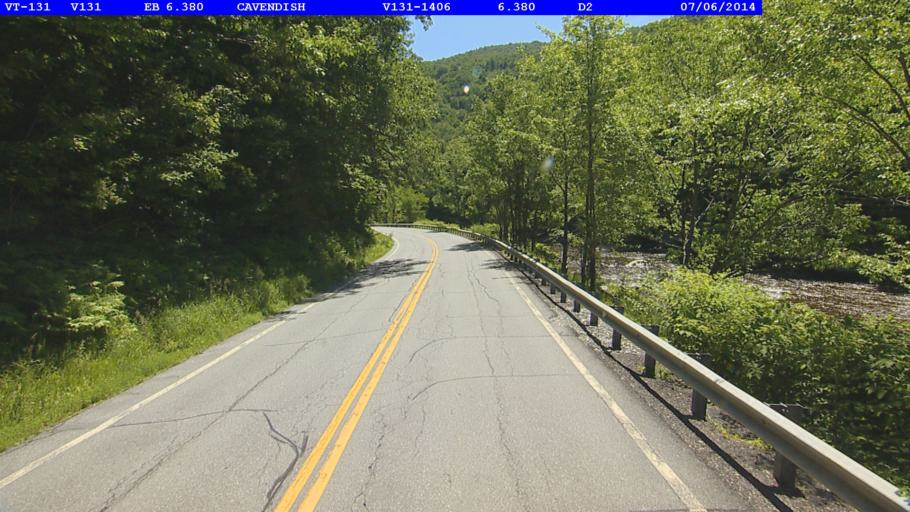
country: US
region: Vermont
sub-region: Windsor County
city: Springfield
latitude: 43.3889
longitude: -72.5589
